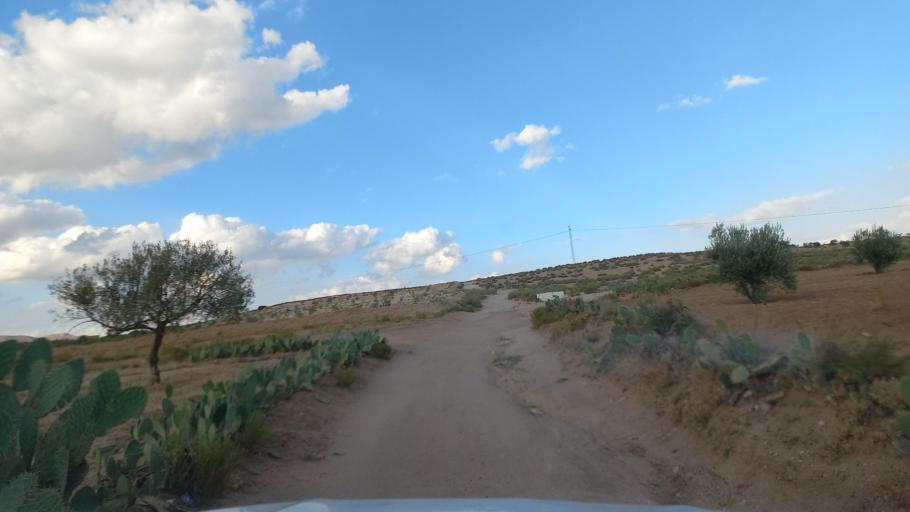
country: TN
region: Al Qasrayn
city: Sbiba
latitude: 35.3880
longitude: 9.0544
